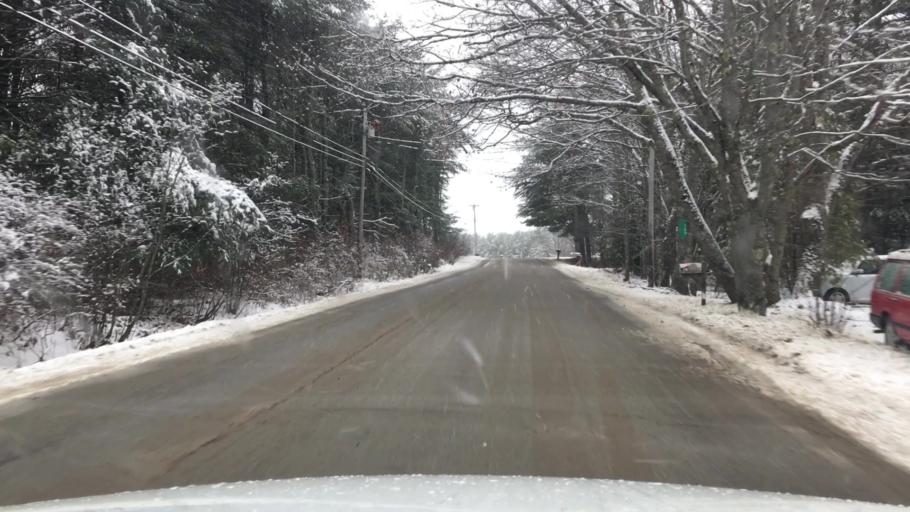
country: US
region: Maine
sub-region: Knox County
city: Union
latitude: 44.1646
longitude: -69.3122
